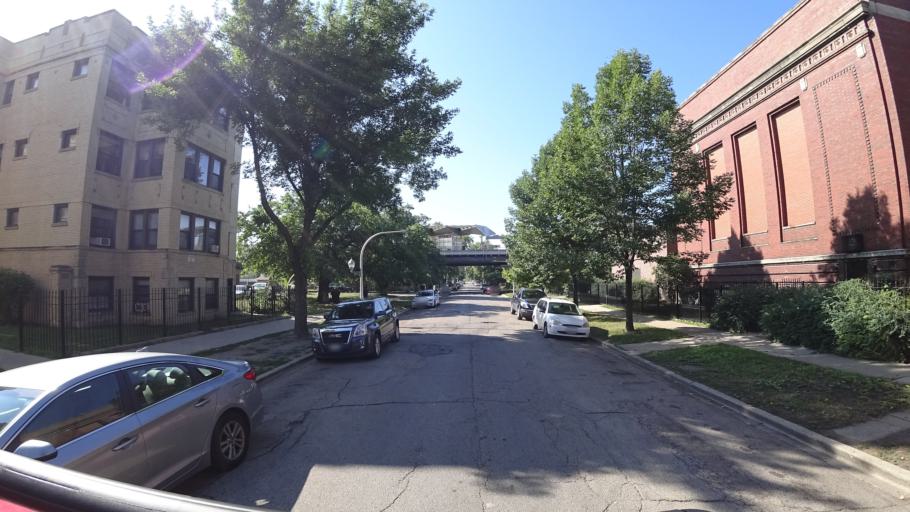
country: US
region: Illinois
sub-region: Cook County
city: Cicero
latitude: 41.8544
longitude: -87.7236
